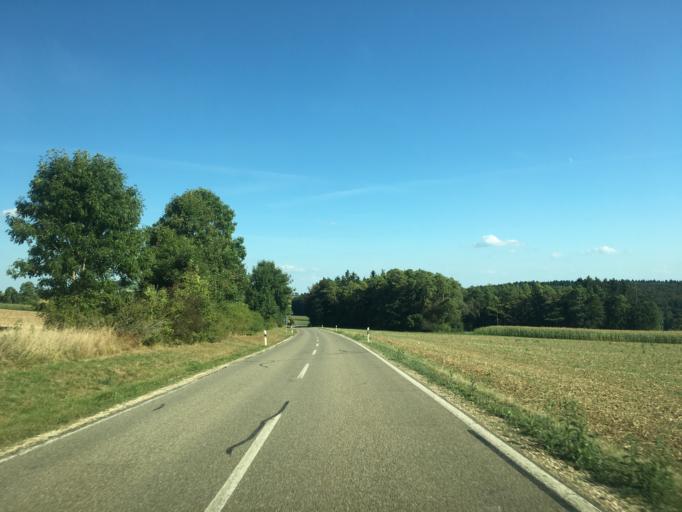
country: DE
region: Baden-Wuerttemberg
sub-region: Tuebingen Region
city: Emeringen
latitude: 48.2543
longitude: 9.5235
